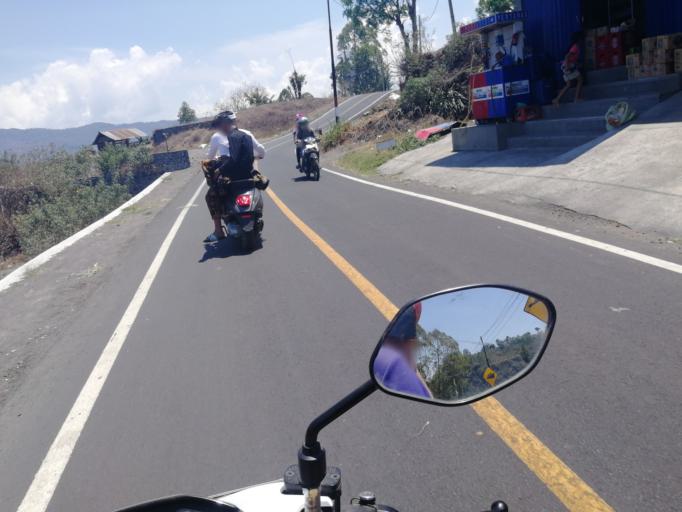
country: ID
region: Bali
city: Banjar Trunyan
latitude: -8.2315
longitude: 115.4063
